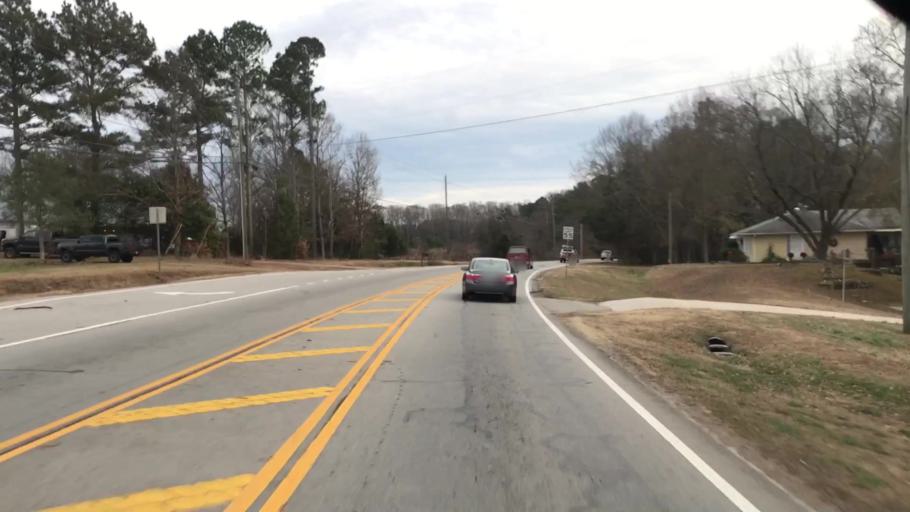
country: US
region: Georgia
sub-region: Barrow County
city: Winder
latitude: 34.0211
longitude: -83.7635
